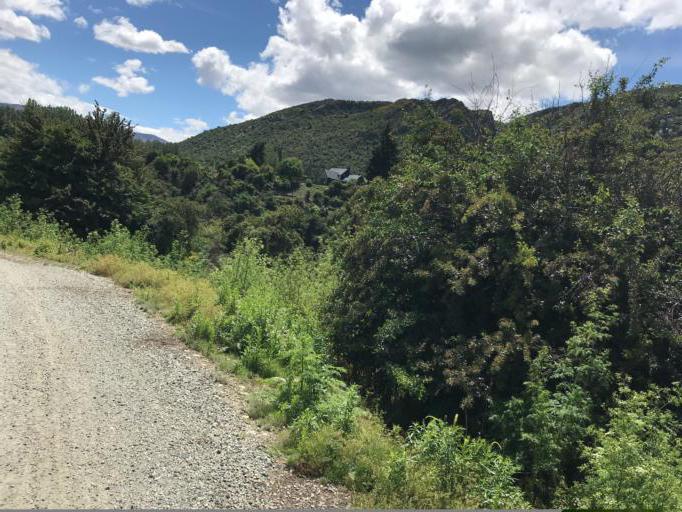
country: NZ
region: Otago
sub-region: Queenstown-Lakes District
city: Arrowtown
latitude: -44.9934
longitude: 168.8618
